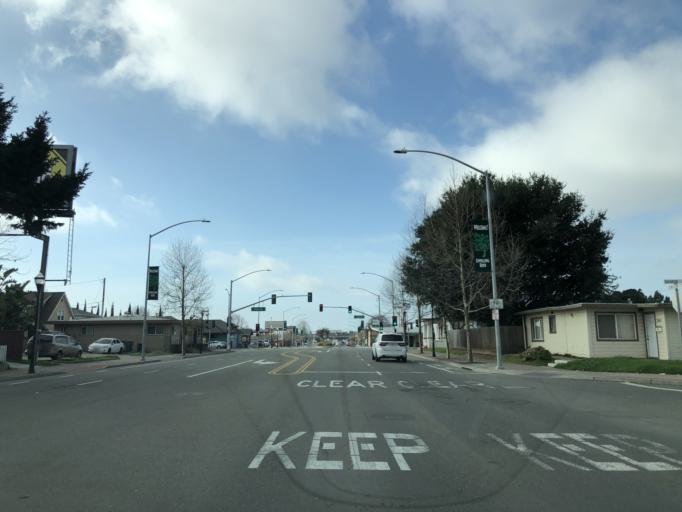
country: US
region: California
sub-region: Alameda County
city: San Lorenzo
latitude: 37.6865
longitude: -122.1268
